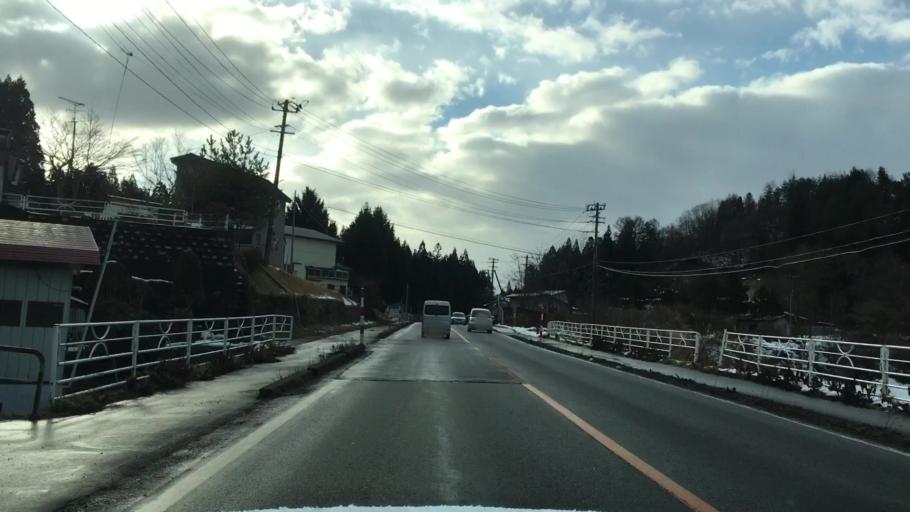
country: JP
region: Akita
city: Odate
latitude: 40.3294
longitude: 140.5823
